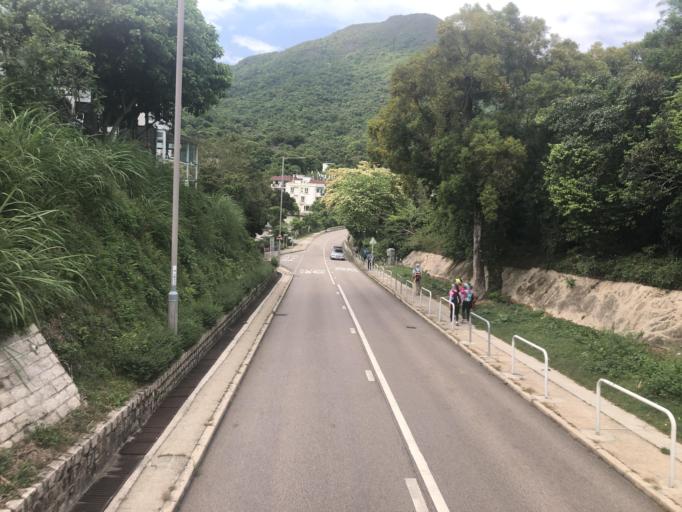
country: HK
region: Sai Kung
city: Sai Kung
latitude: 22.3907
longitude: 114.3078
